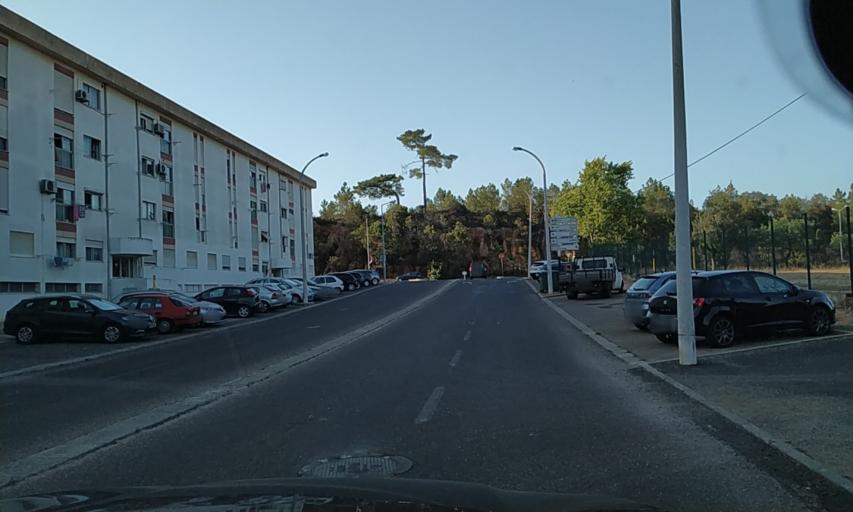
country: PT
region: Setubal
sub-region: Setubal
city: Setubal
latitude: 38.5219
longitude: -8.8598
